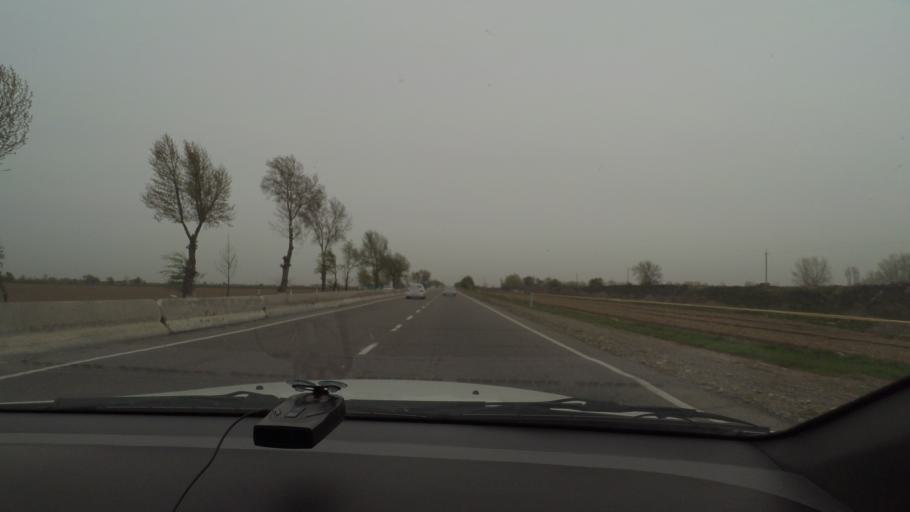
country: UZ
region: Jizzax
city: Gagarin
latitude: 40.5419
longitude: 68.3525
